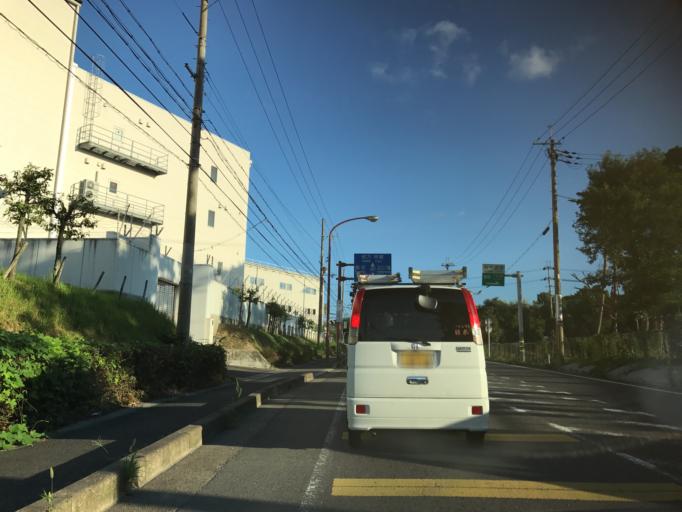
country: JP
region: Shiga Prefecture
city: Youkaichi
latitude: 35.0895
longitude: 136.2500
